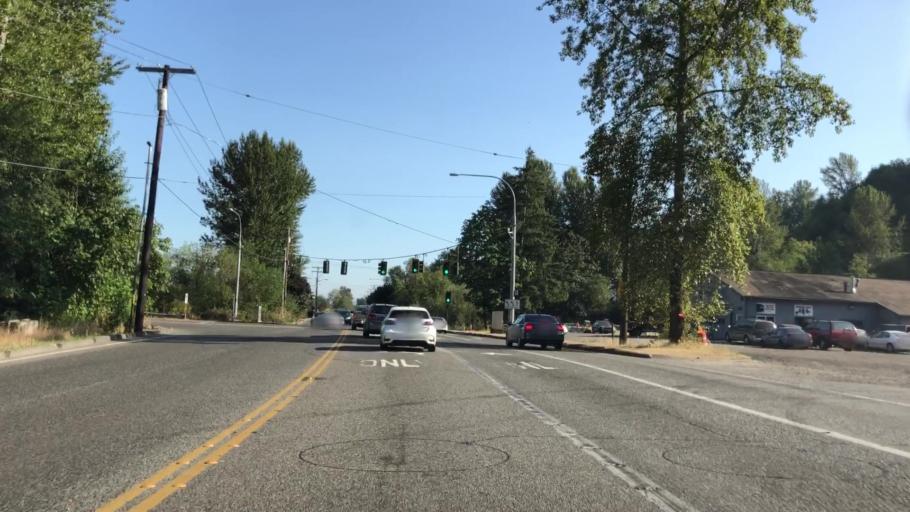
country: US
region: Washington
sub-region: King County
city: Algona
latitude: 47.2964
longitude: -122.2605
